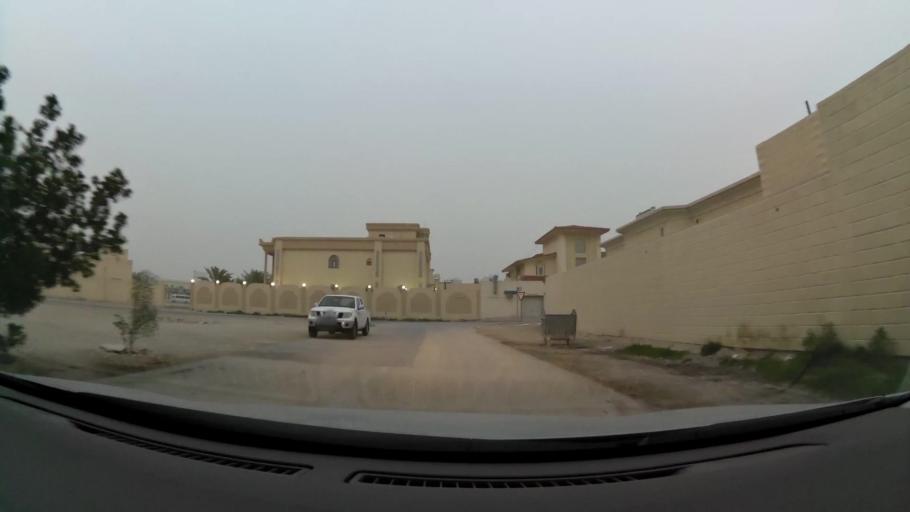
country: QA
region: Baladiyat ad Dawhah
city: Doha
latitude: 25.2308
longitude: 51.4931
